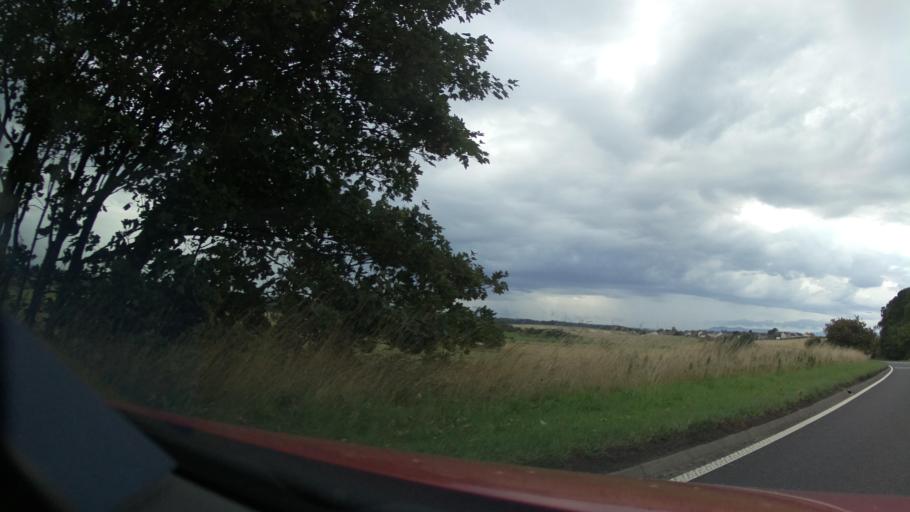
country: GB
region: Scotland
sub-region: Fife
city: Cairneyhill
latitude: 56.0556
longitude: -3.5417
